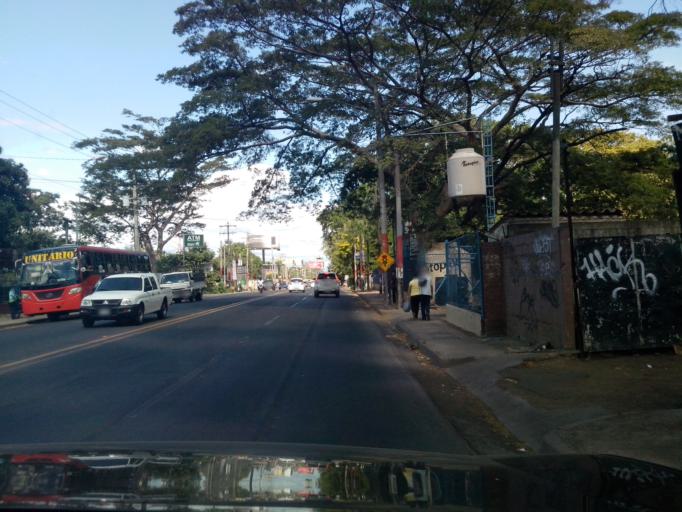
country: NI
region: Managua
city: Ciudad Sandino
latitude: 12.1262
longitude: -86.3122
